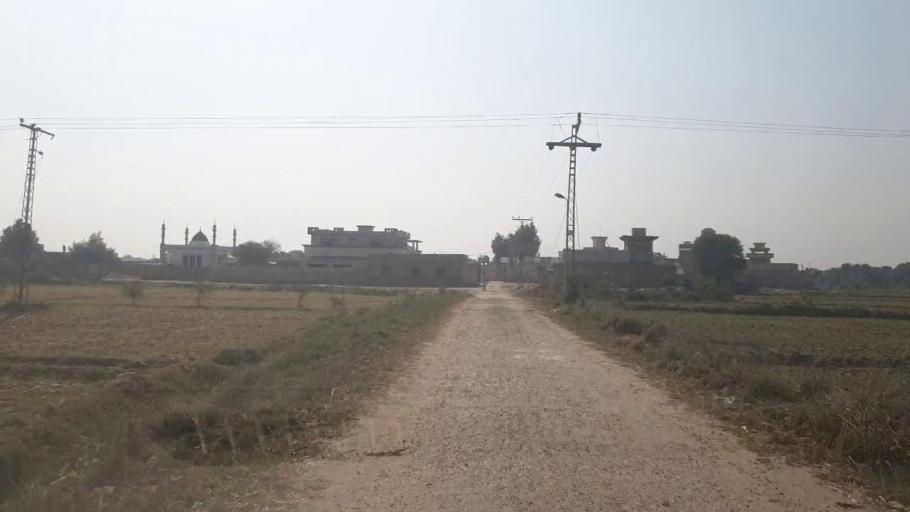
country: PK
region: Sindh
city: Tando Allahyar
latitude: 25.4799
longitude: 68.7910
